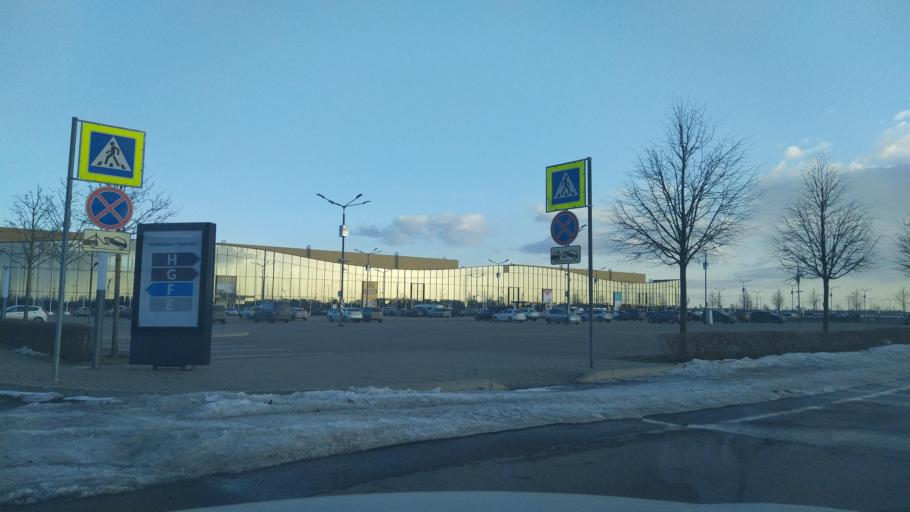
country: RU
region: St.-Petersburg
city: Aleksandrovskaya
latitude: 59.7623
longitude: 30.3513
